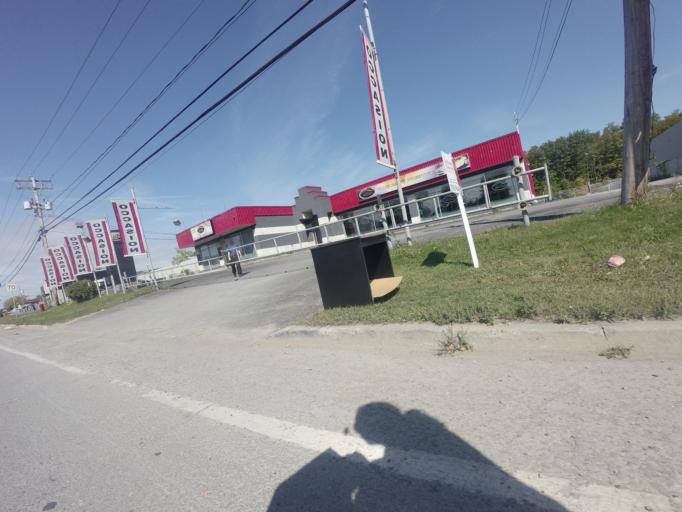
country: CA
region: Quebec
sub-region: Laurentides
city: Saint-Eustache
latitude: 45.5830
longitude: -73.9227
